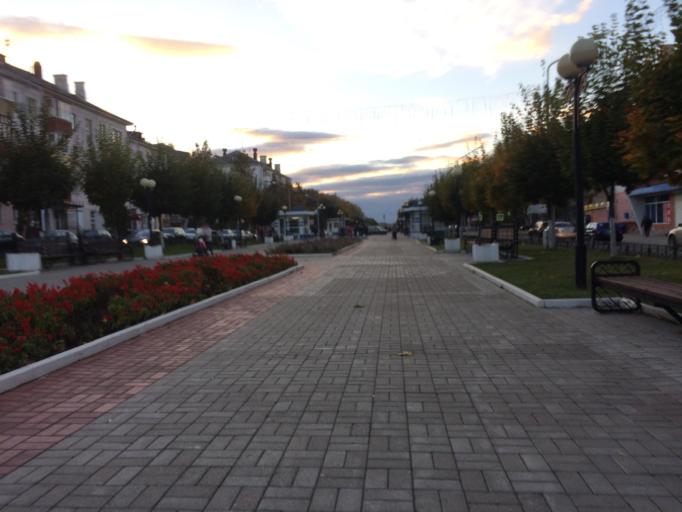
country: RU
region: Mariy-El
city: Yoshkar-Ola
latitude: 56.6379
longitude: 47.8838
